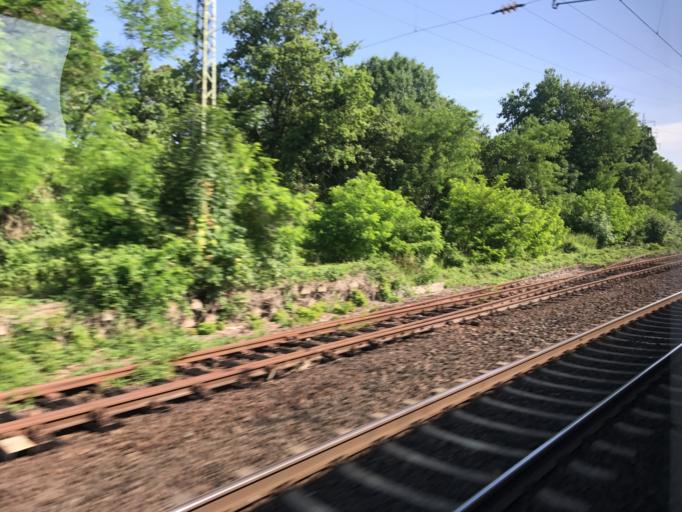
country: DE
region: Hesse
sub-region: Regierungsbezirk Darmstadt
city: Eltville
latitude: 50.0080
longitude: 8.1377
